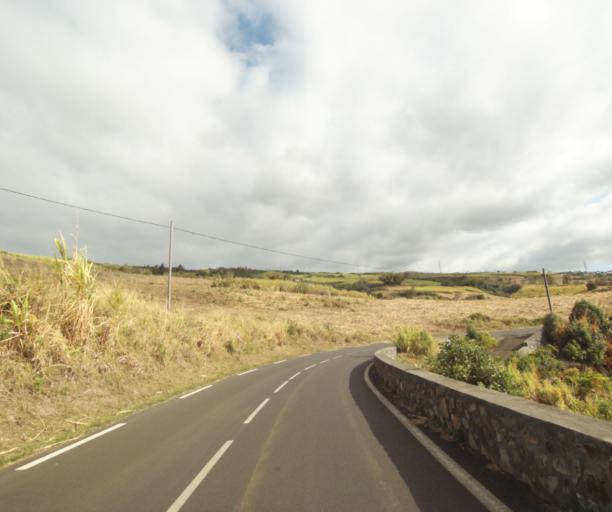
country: RE
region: Reunion
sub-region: Reunion
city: Saint-Paul
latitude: -21.0196
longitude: 55.3141
